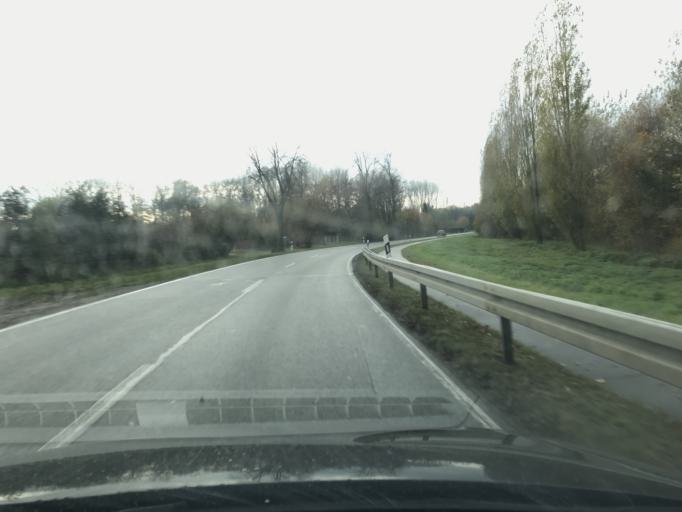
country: DE
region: North Rhine-Westphalia
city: Oelde
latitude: 51.8360
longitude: 8.1731
